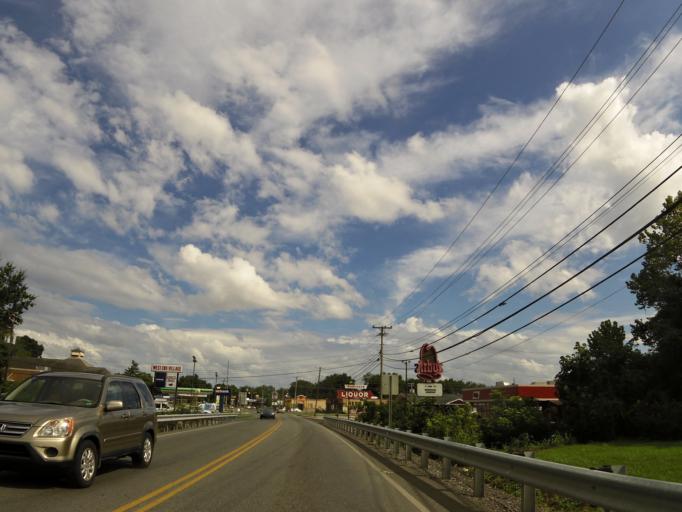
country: US
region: Kentucky
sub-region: Christian County
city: Hopkinsville
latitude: 36.8724
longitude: -87.5013
